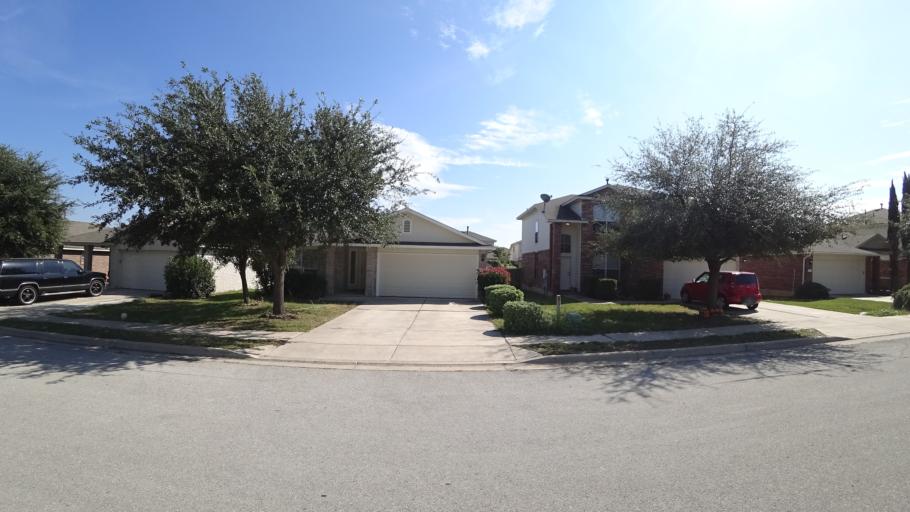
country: US
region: Texas
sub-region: Travis County
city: Pflugerville
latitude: 30.4233
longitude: -97.6361
